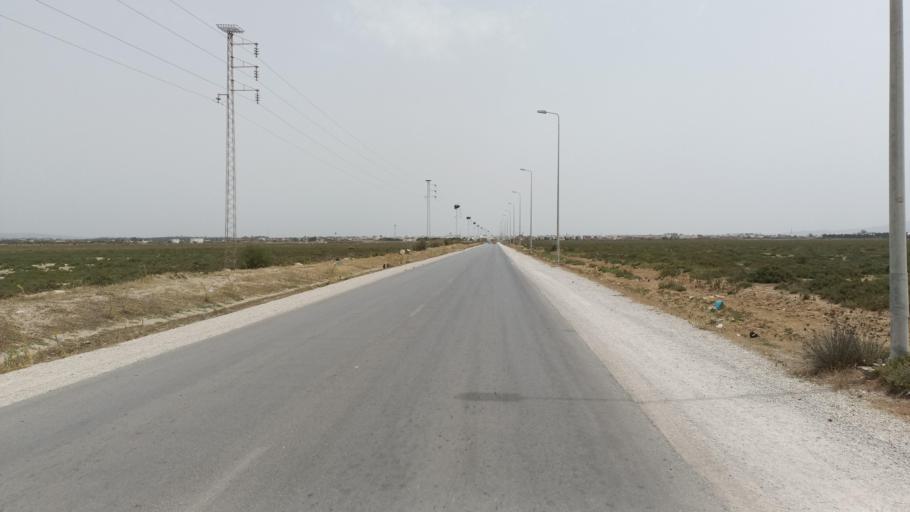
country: TN
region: Nabul
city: Manzil Bu Zalafah
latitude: 36.7210
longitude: 10.4742
